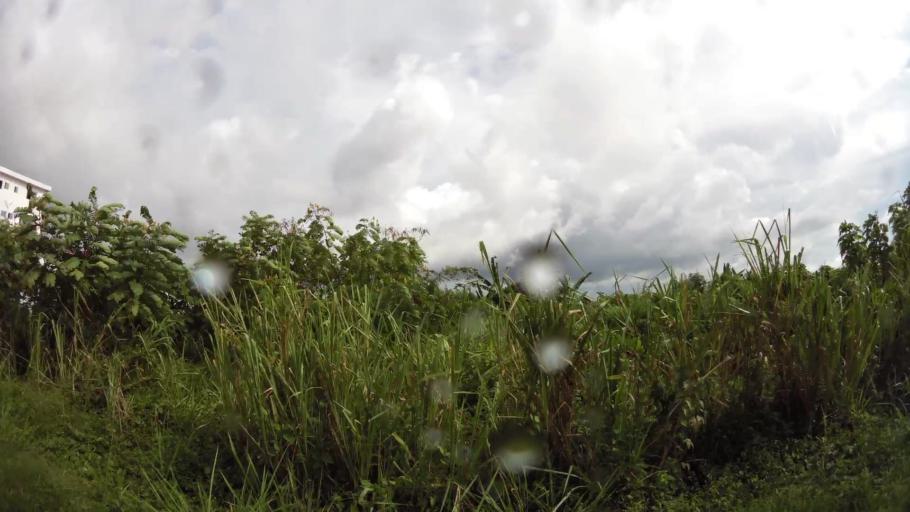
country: SR
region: Paramaribo
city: Paramaribo
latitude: 5.8420
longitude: -55.2000
